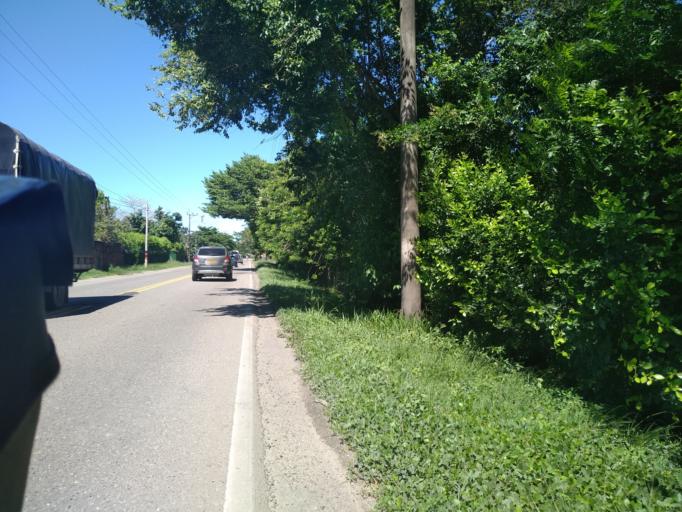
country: CO
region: Cundinamarca
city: Puerto Salgar
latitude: 5.4775
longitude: -74.6454
